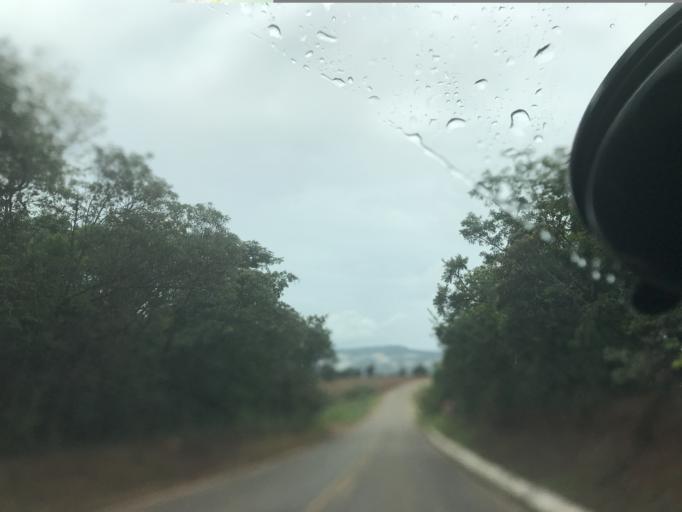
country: BR
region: Minas Gerais
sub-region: Conceicao Do Rio Verde
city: Conceicao do Rio Verde
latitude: -21.6886
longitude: -45.0115
